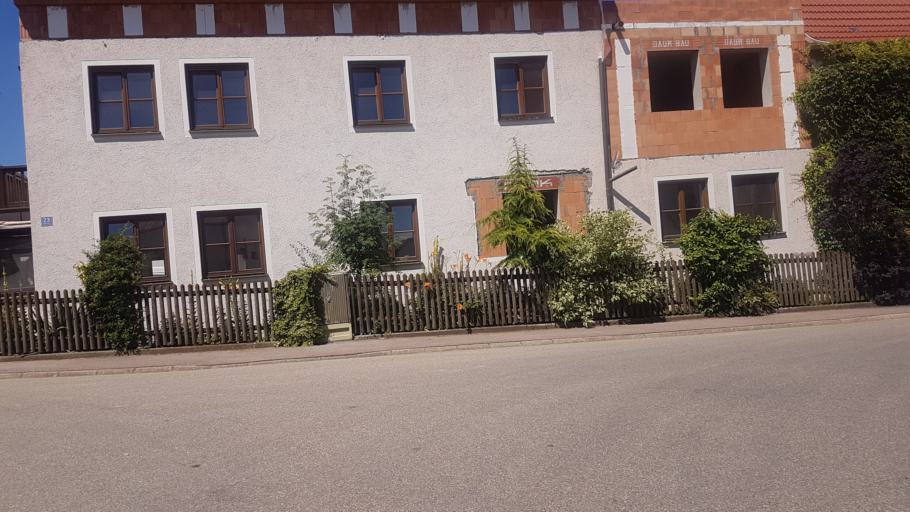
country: DE
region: Bavaria
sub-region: Upper Bavaria
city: Vohburg an der Donau
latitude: 48.7793
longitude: 11.6391
